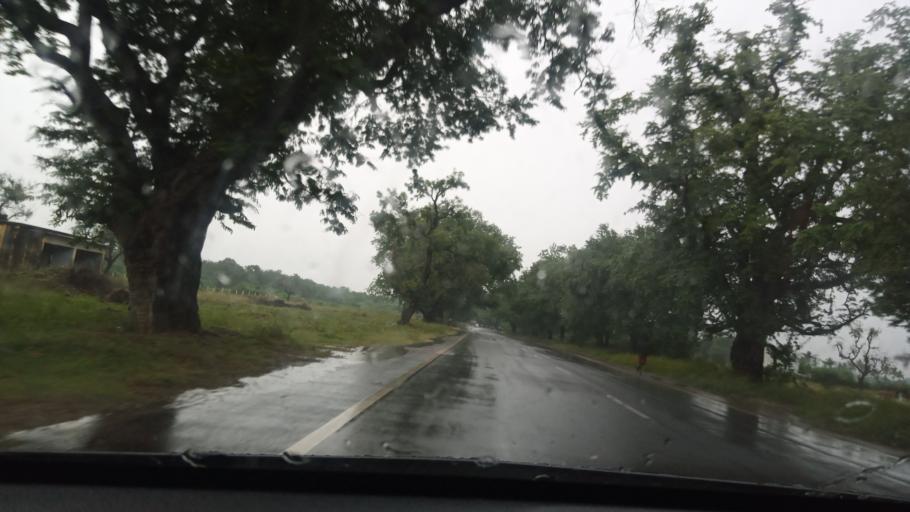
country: IN
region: Tamil Nadu
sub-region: Vellore
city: Kalavai
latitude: 12.8051
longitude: 79.4231
